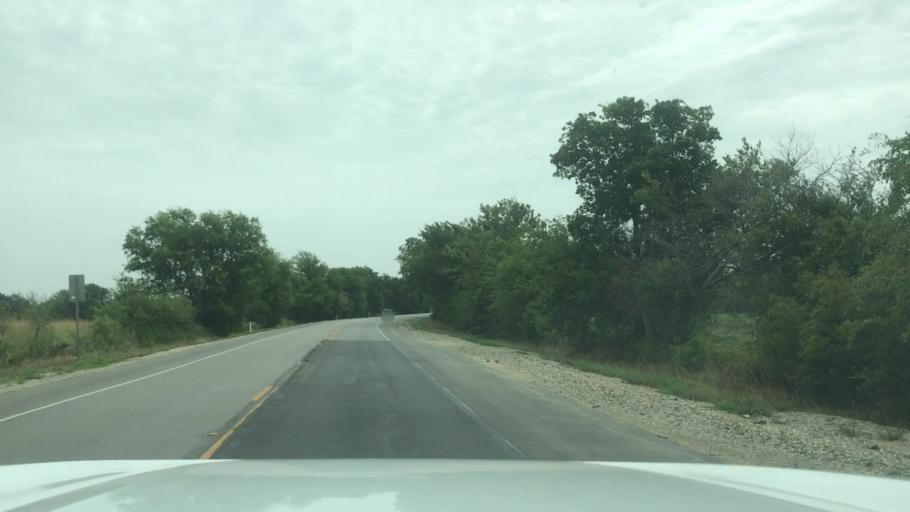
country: US
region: Texas
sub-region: Erath County
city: Dublin
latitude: 32.0918
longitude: -98.2710
